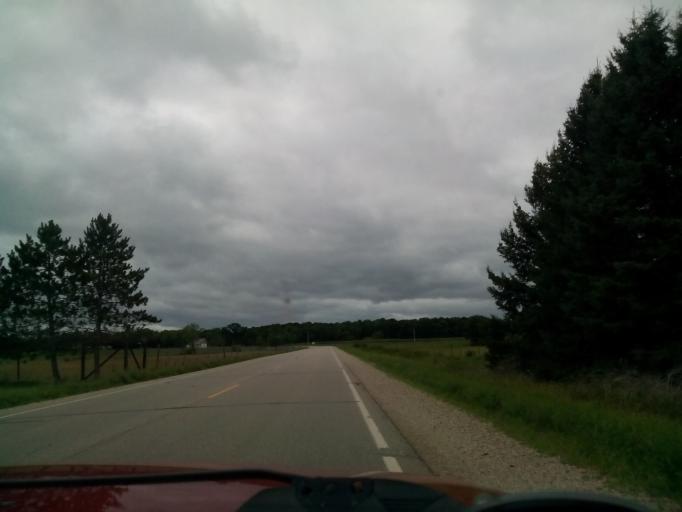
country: US
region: Wisconsin
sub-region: Menominee County
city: Legend Lake
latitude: 44.9981
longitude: -88.4321
